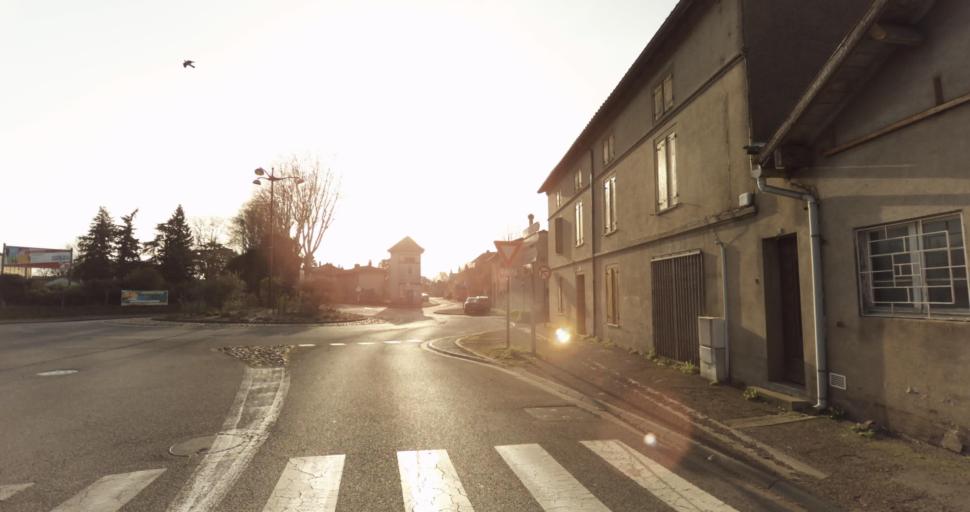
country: FR
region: Midi-Pyrenees
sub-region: Departement du Tarn
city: Saint-Sulpice-la-Pointe
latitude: 43.7767
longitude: 1.6796
